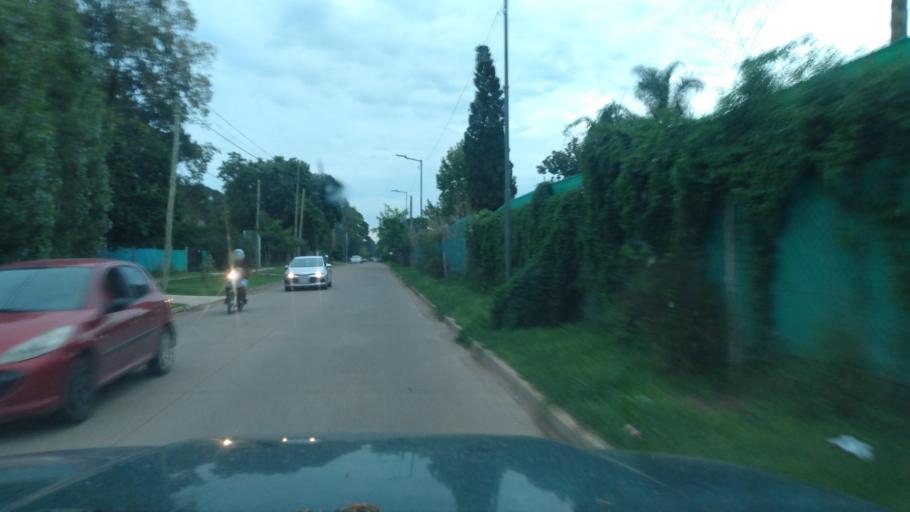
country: AR
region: Buenos Aires
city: Hurlingham
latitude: -34.5700
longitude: -58.7105
